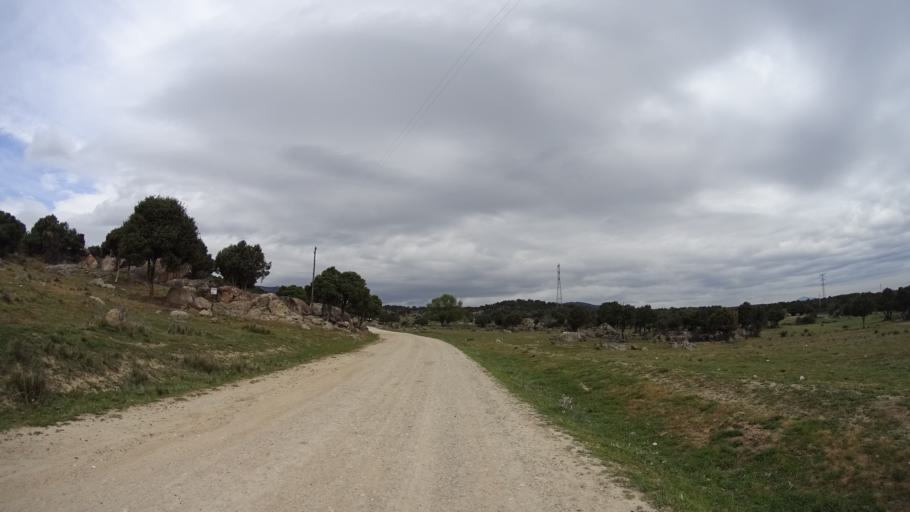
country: ES
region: Madrid
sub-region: Provincia de Madrid
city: Hoyo de Manzanares
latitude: 40.6097
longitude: -3.8771
